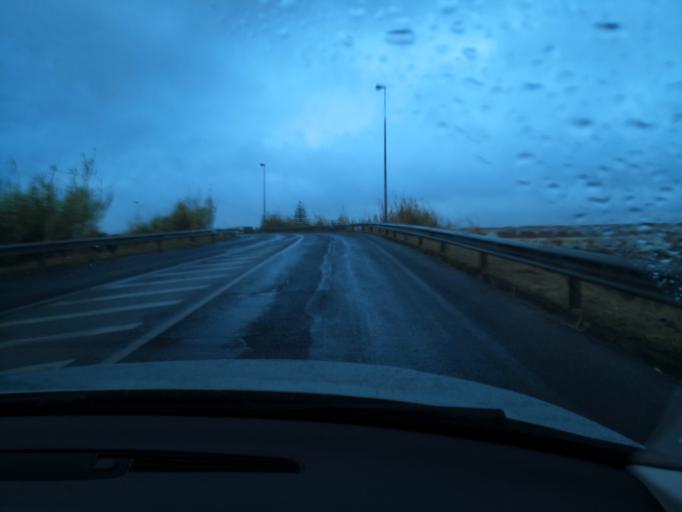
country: PT
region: Setubal
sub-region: Moita
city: Alhos Vedros
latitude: 38.6523
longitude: -9.0307
